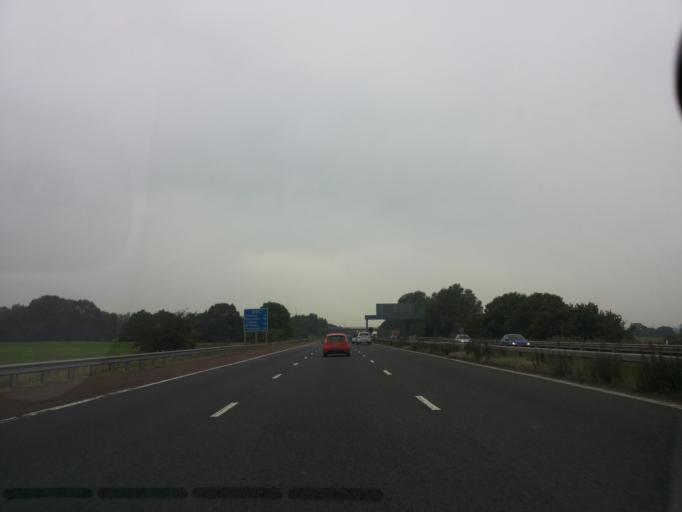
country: GB
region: England
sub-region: Lancashire
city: Preston
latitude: 53.7995
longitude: -2.7268
